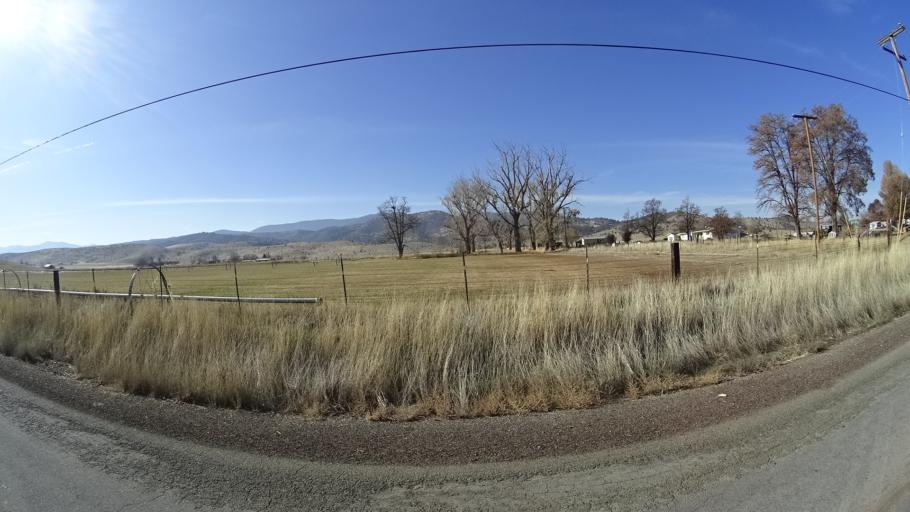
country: US
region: California
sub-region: Siskiyou County
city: Montague
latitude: 41.6178
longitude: -122.5228
